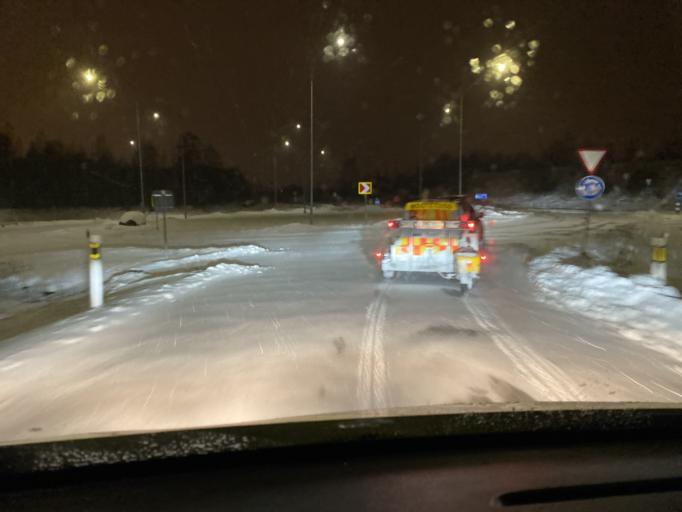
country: EE
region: Harju
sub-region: Maardu linn
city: Maardu
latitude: 59.4531
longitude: 25.0311
